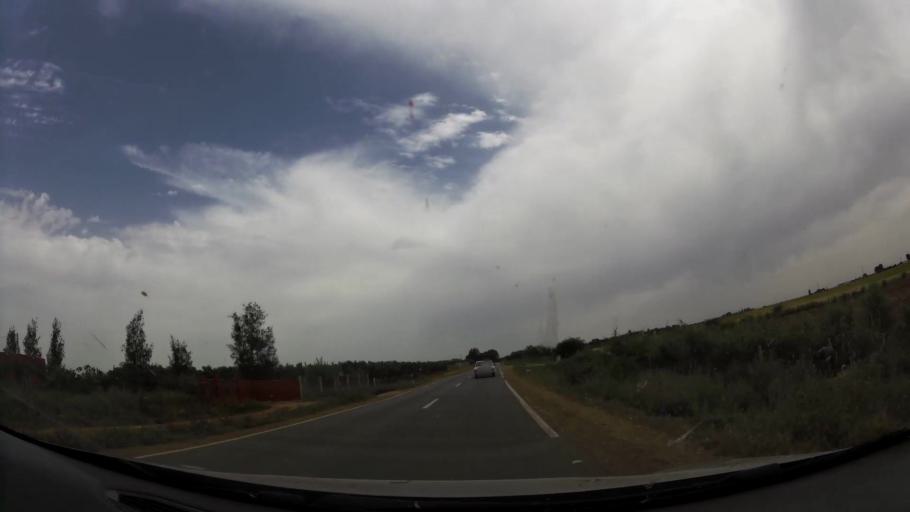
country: MA
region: Rabat-Sale-Zemmour-Zaer
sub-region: Khemisset
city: Tiflet
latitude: 33.8286
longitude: -6.2718
